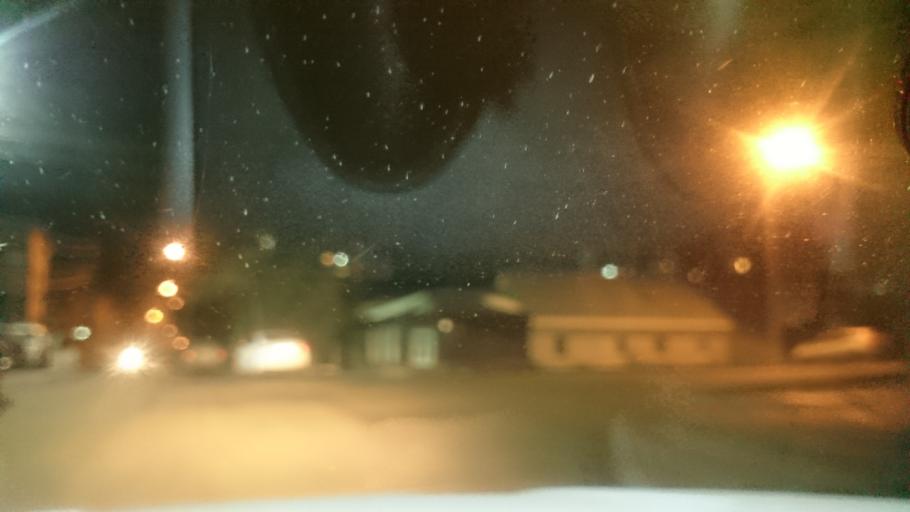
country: RU
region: Tula
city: Tula
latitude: 54.1826
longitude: 37.6323
